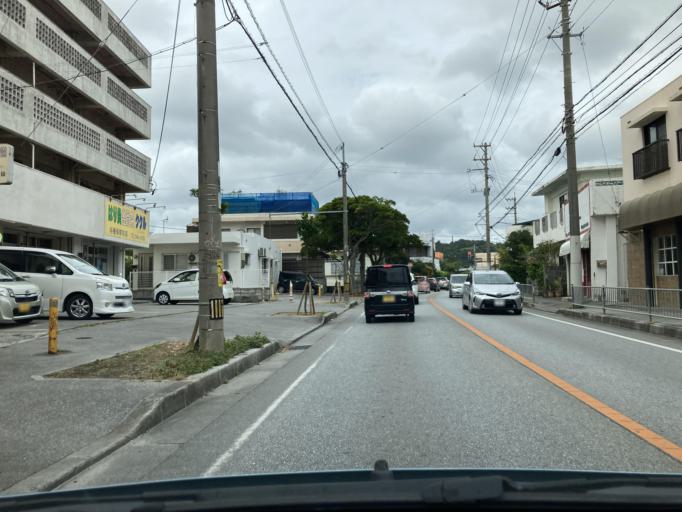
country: JP
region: Okinawa
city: Ginowan
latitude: 26.2261
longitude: 127.7570
